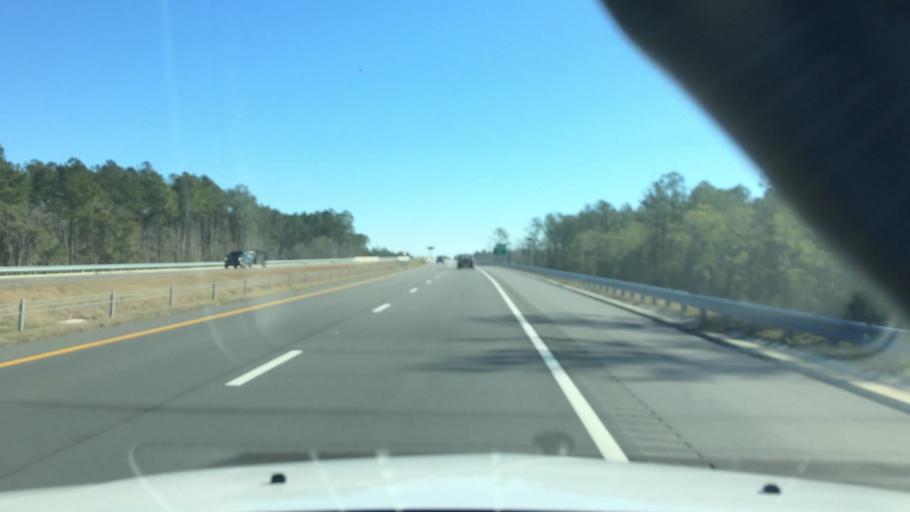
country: US
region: North Carolina
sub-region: Brunswick County
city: Leland
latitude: 34.2728
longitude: -78.0261
